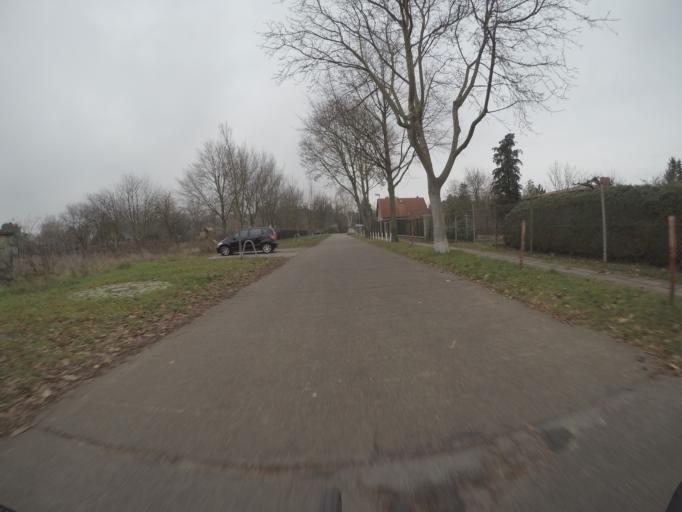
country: DE
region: Berlin
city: Biesdorf
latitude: 52.4868
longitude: 13.5681
